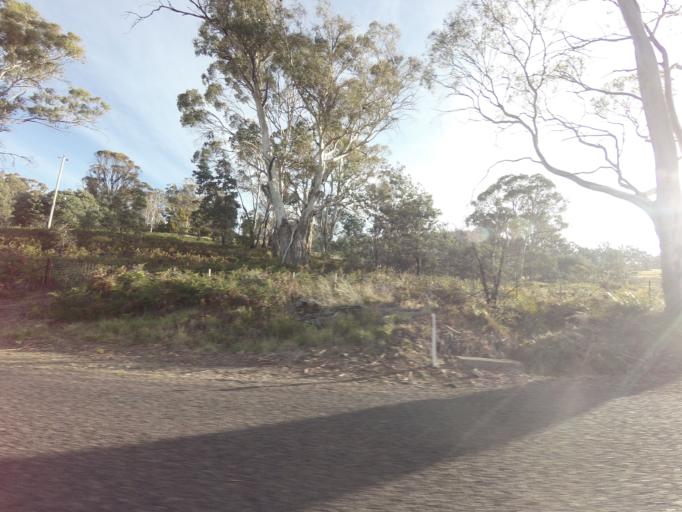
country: AU
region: Tasmania
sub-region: Brighton
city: Bridgewater
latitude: -42.4112
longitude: 147.1234
